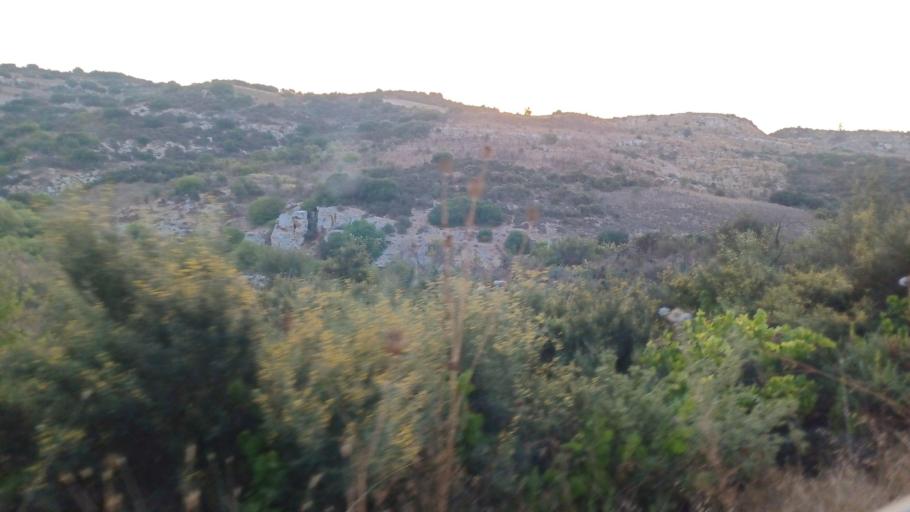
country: CY
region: Pafos
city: Mesogi
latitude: 34.8714
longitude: 32.5314
